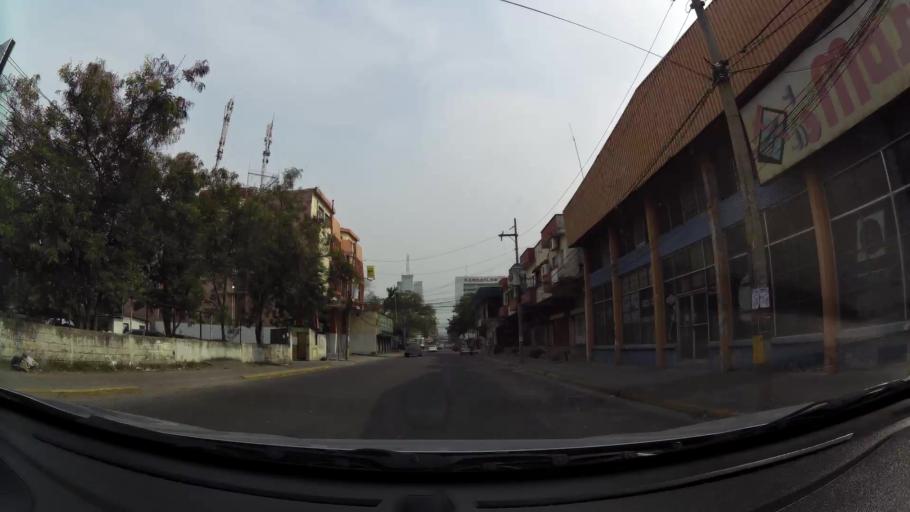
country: HN
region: Cortes
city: San Pedro Sula
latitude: 15.5091
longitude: -88.0242
